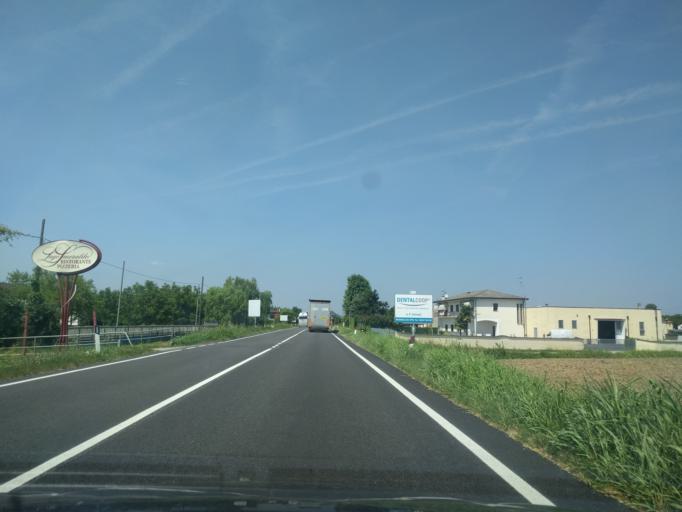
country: IT
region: Veneto
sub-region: Provincia di Padova
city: Solesino
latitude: 45.1883
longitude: 11.7559
